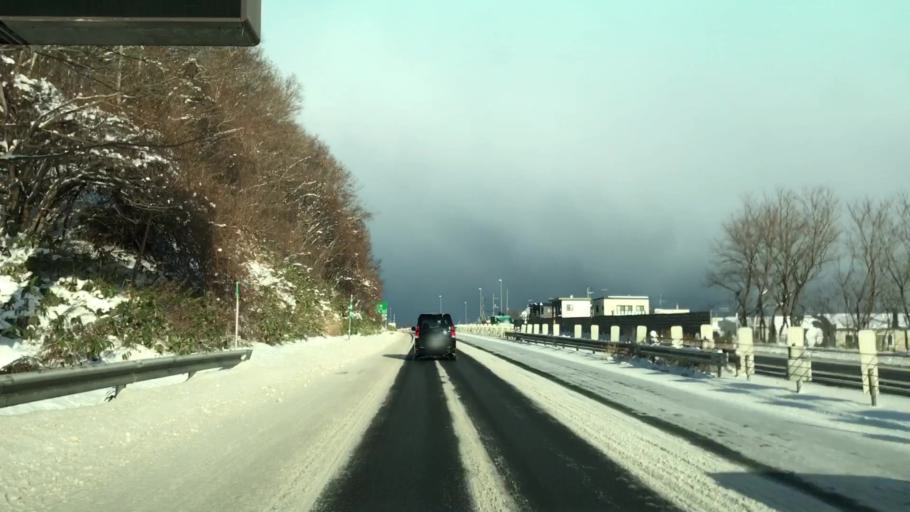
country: JP
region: Hokkaido
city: Sapporo
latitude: 43.1073
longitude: 141.2419
